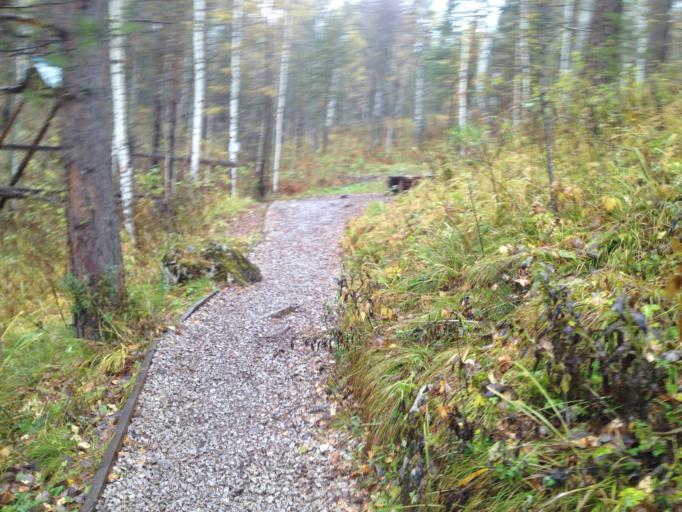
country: RU
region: Sverdlovsk
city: Nizhniye Sergi
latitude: 56.5176
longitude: 59.2552
